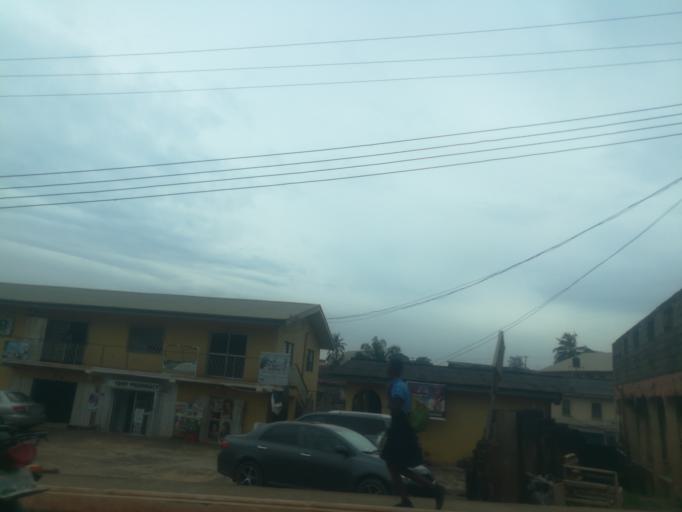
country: NG
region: Oyo
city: Ibadan
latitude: 7.3927
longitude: 3.9289
